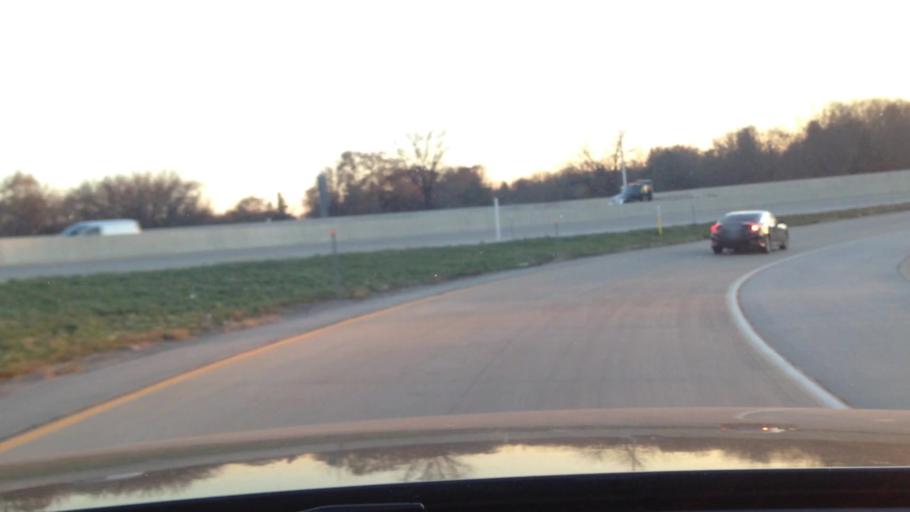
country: US
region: Illinois
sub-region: Kane County
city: East Dundee
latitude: 42.0655
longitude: -88.2589
